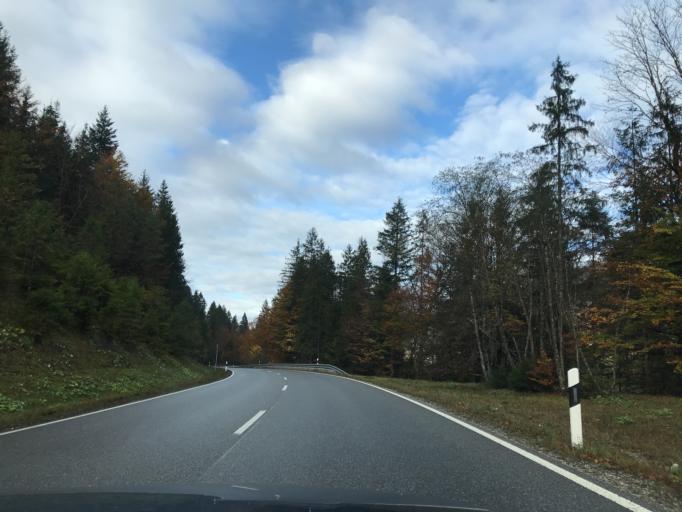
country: DE
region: Bavaria
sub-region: Upper Bavaria
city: Jachenau
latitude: 47.5586
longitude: 11.4871
